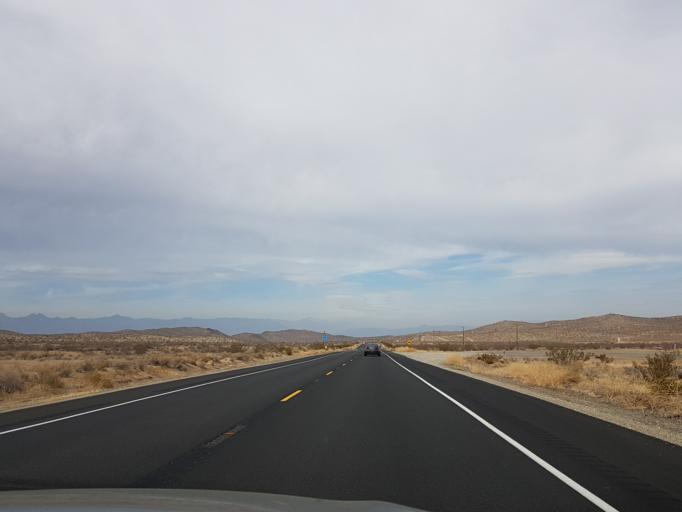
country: US
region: California
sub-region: Kern County
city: Ridgecrest
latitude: 35.5100
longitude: -117.6685
